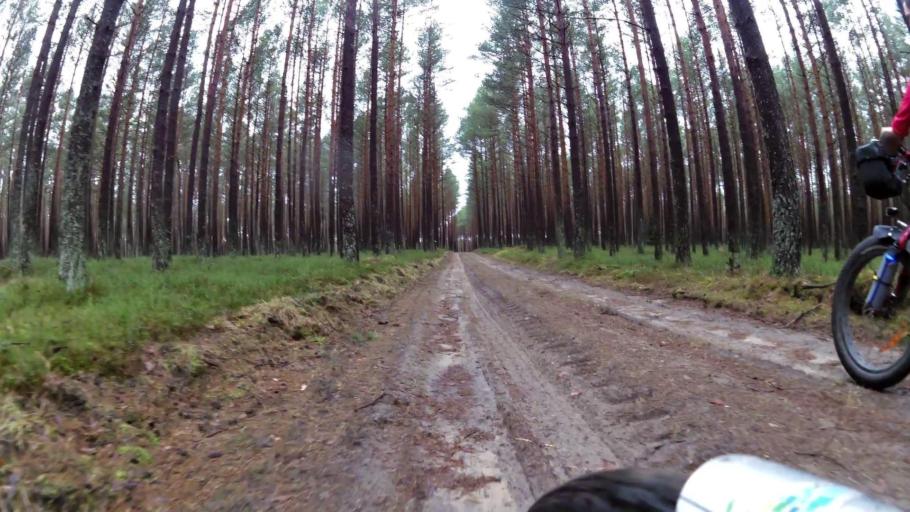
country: PL
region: Pomeranian Voivodeship
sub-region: Powiat bytowski
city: Borzytuchom
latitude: 54.2673
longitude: 17.4051
